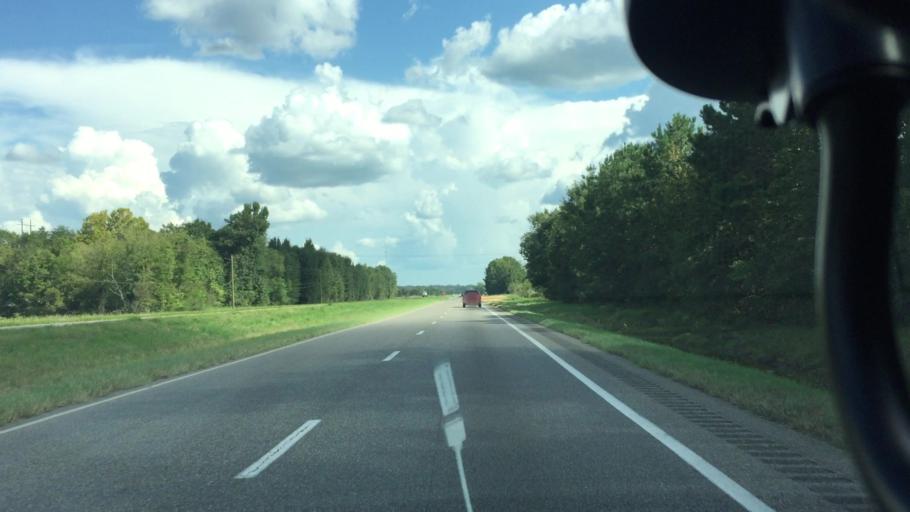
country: US
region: Alabama
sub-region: Montgomery County
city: Pike Road
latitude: 32.2400
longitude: -86.1310
